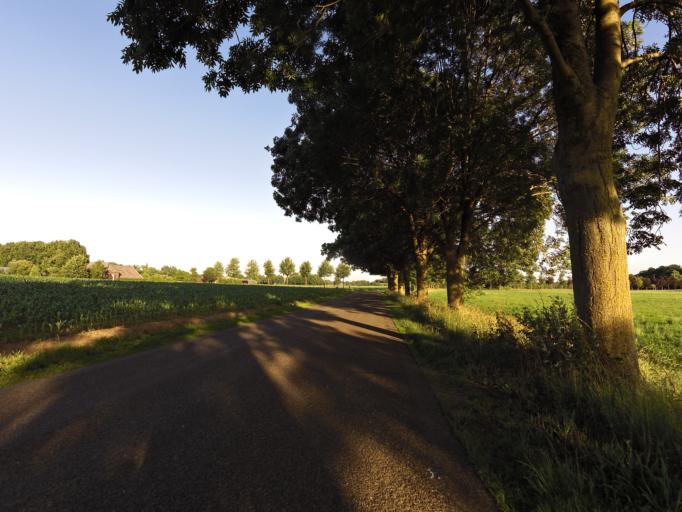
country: DE
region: North Rhine-Westphalia
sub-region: Regierungsbezirk Munster
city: Isselburg
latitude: 51.8698
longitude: 6.4284
